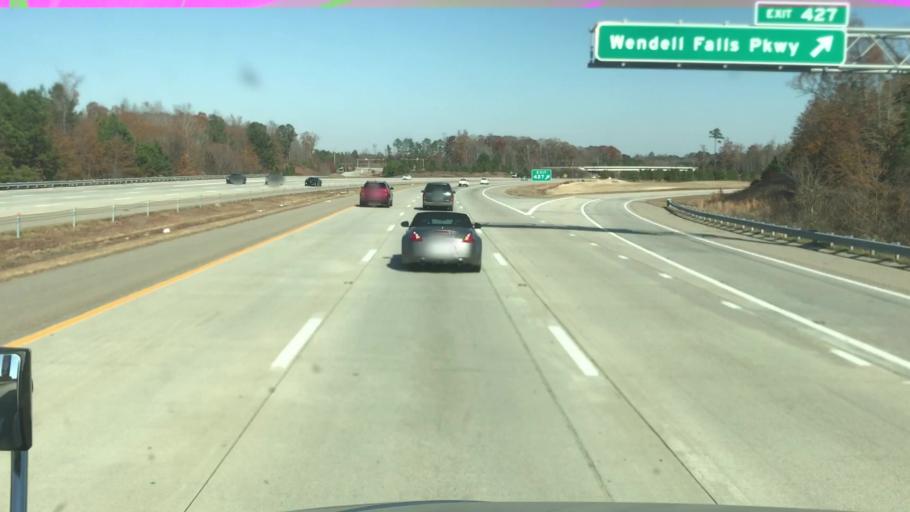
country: US
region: North Carolina
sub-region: Wake County
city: Knightdale
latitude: 35.7782
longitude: -78.4454
